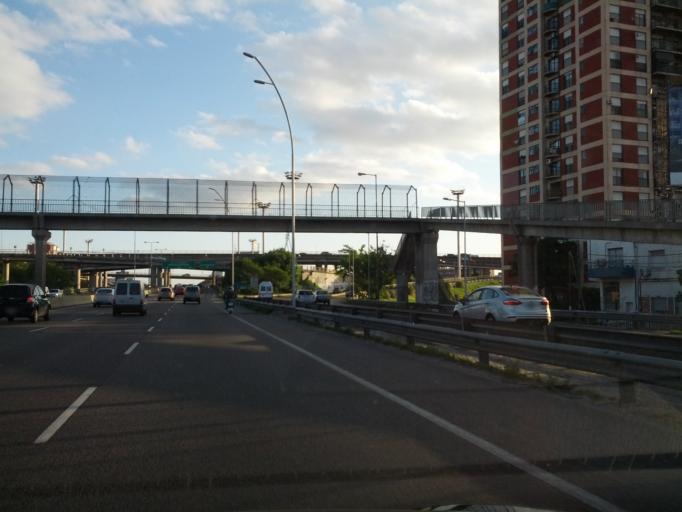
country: AR
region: Buenos Aires
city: Caseros
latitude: -34.6325
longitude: -58.5302
